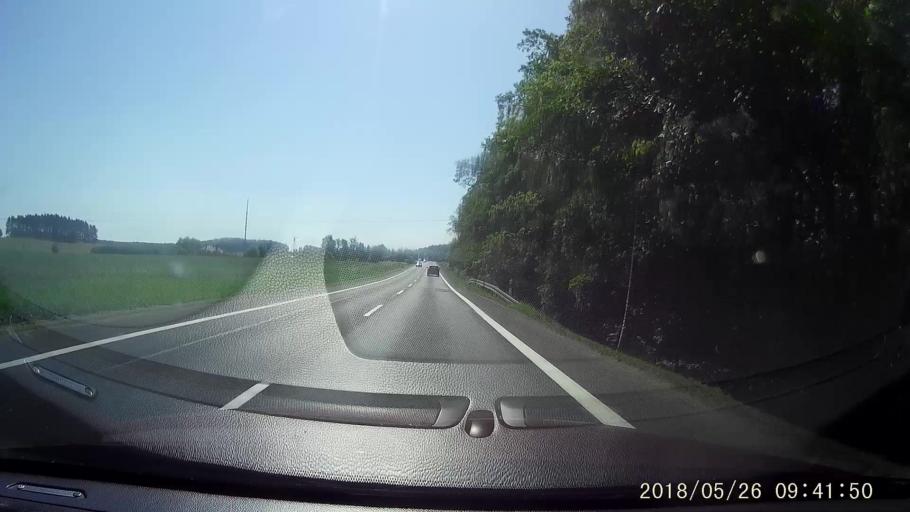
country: PL
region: Lower Silesian Voivodeship
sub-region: Powiat lubanski
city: Siekierczyn
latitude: 51.1611
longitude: 15.1519
